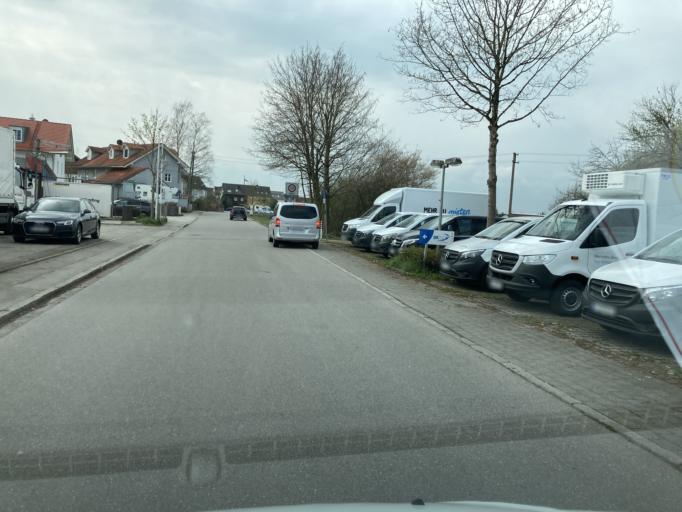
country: DE
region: Bavaria
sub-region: Upper Bavaria
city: Grafing bei Munchen
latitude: 48.0546
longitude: 11.9586
